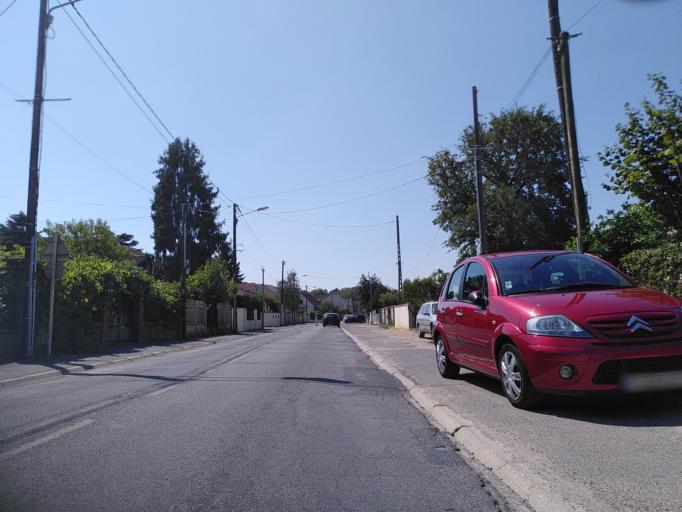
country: FR
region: Ile-de-France
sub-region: Departement de l'Essonne
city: Saint-Germain-les-Arpajon
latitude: 48.5979
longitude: 2.2652
